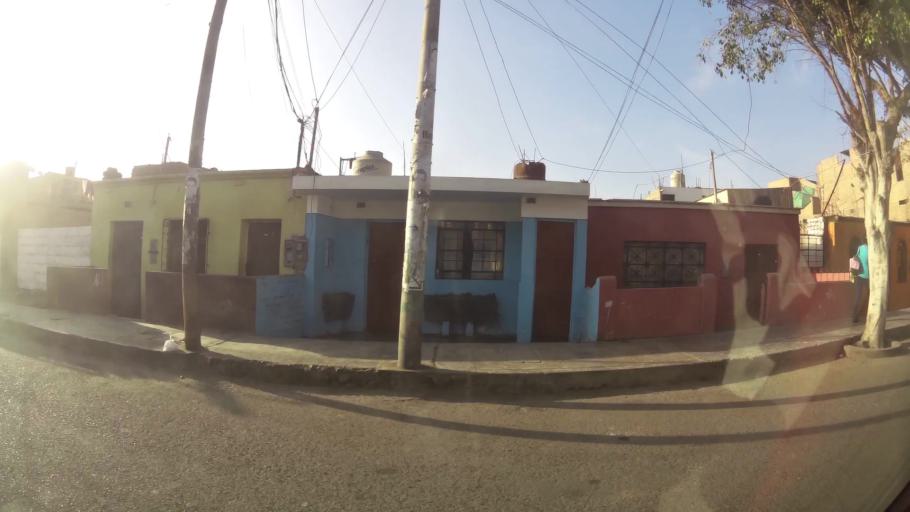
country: PE
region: Lima
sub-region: Huaura
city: Huacho
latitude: -11.1102
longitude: -77.6044
